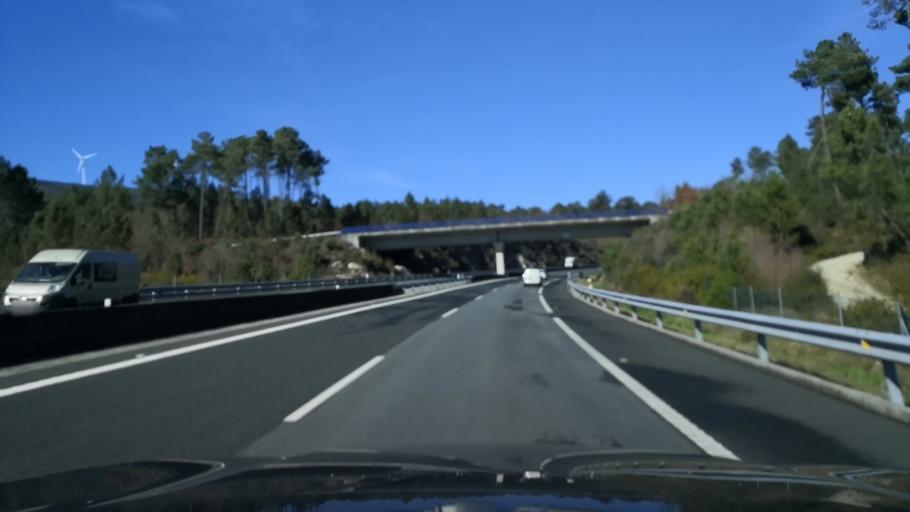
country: ES
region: Galicia
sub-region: Provincia de Ourense
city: Pinor
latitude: 42.4970
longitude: -8.0281
